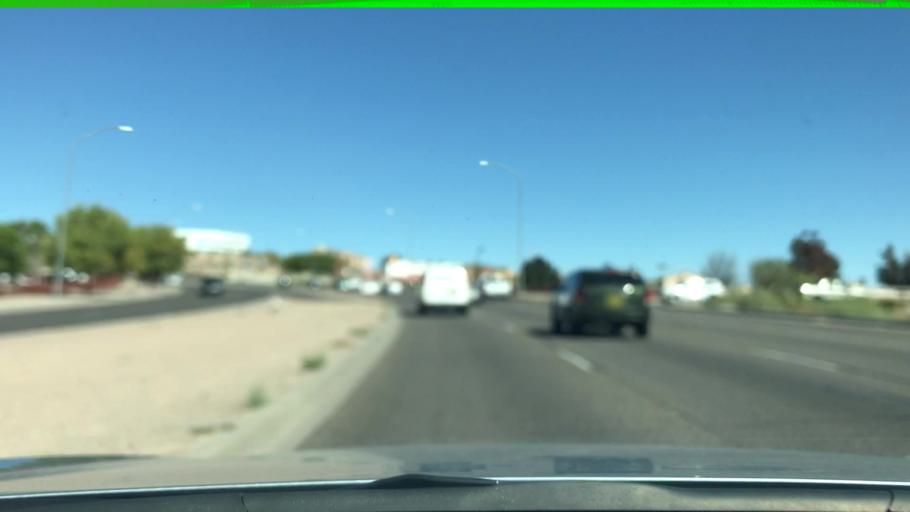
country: US
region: New Mexico
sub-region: Sandoval County
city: Rio Rancho
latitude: 35.2083
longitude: -106.6584
